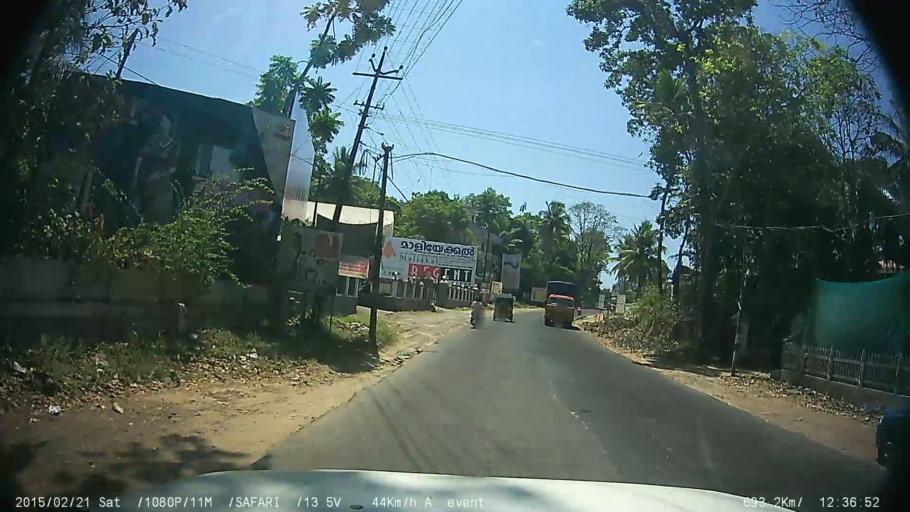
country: IN
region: Kerala
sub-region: Kottayam
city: Kottayam
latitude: 9.6300
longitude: 76.5421
